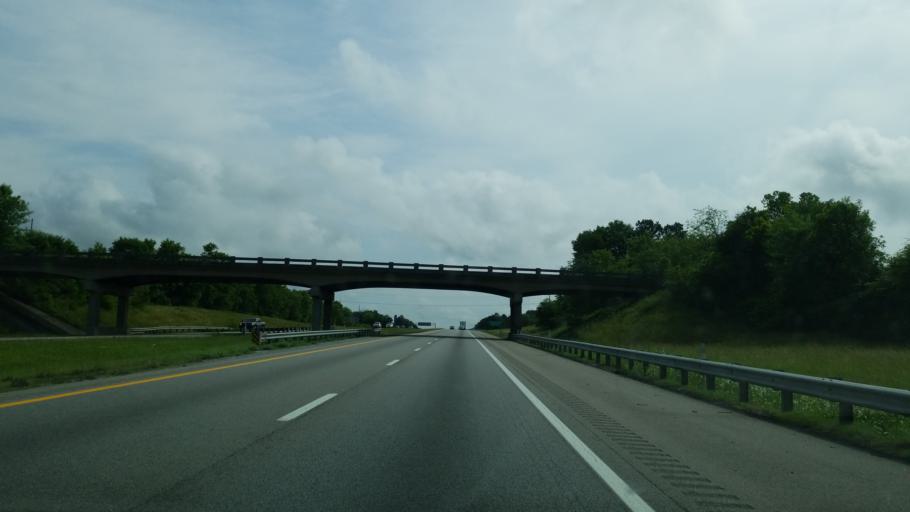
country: US
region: Tennessee
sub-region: Bradley County
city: Cleveland
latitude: 35.1756
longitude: -84.9174
